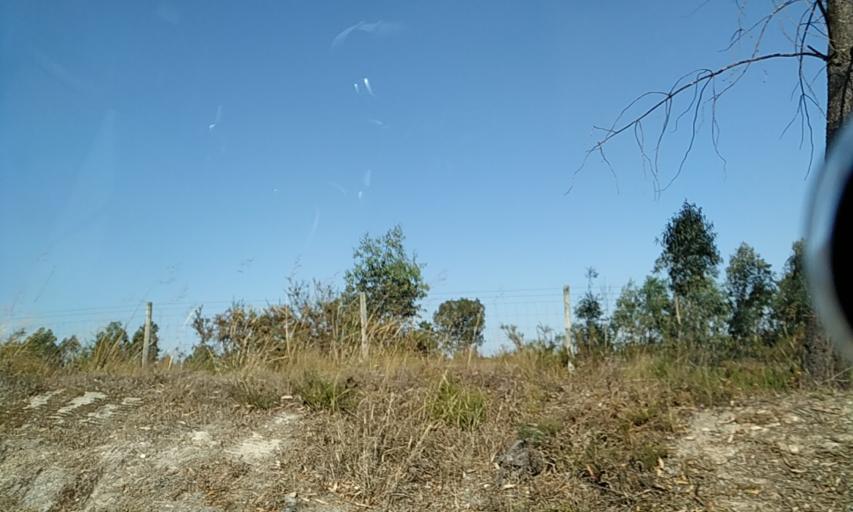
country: PT
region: Santarem
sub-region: Coruche
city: Coruche
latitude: 39.0120
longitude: -8.5631
